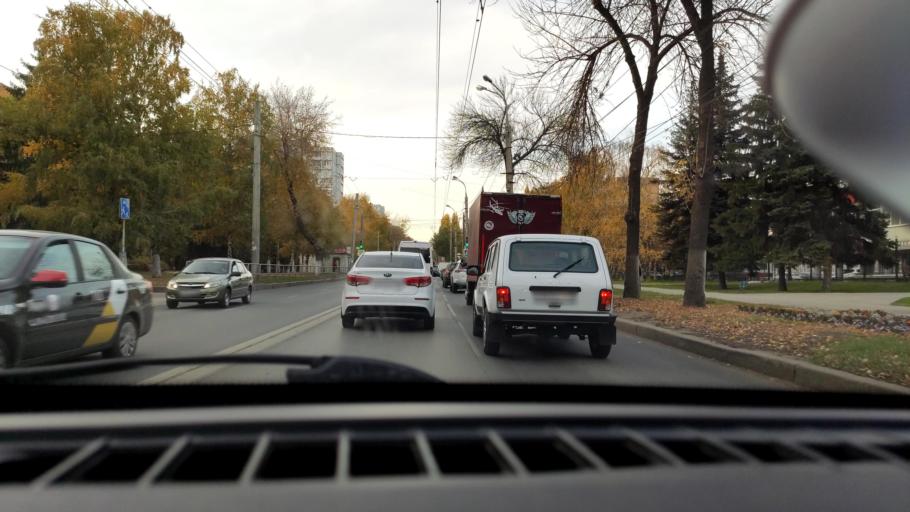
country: RU
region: Samara
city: Samara
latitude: 53.2389
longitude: 50.2380
